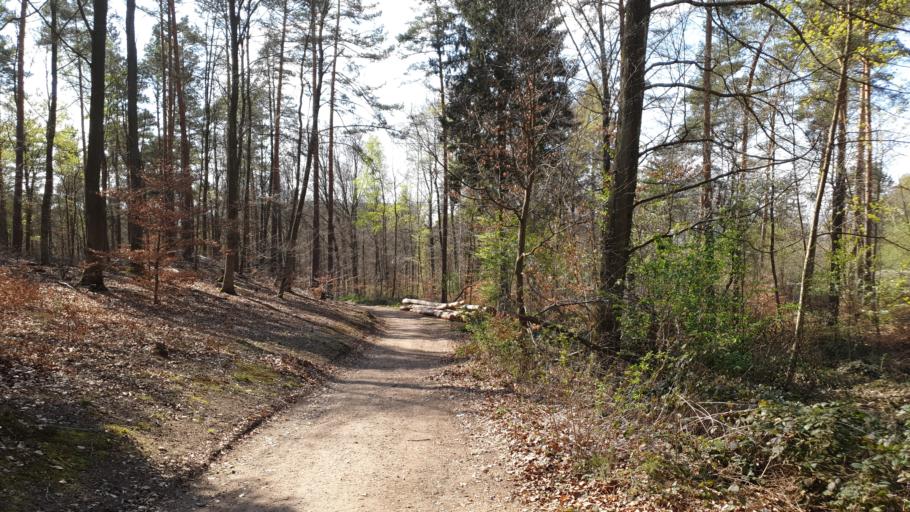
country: DE
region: Rheinland-Pfalz
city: Kaiserslautern
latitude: 49.4352
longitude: 7.7860
